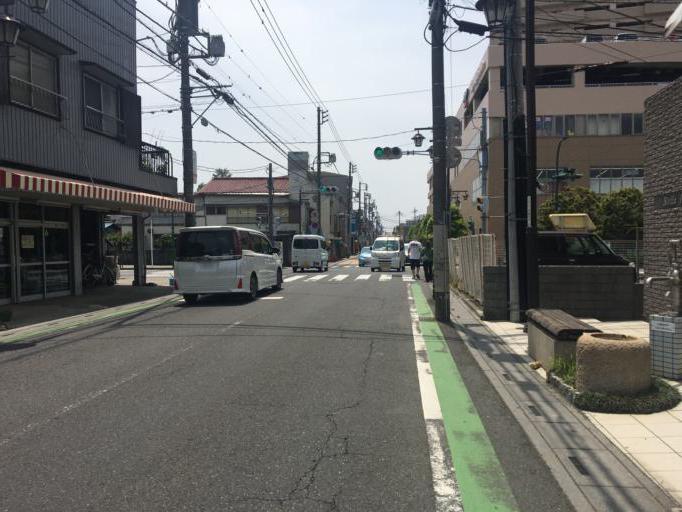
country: JP
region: Saitama
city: Koshigaya
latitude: 35.9030
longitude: 139.7807
